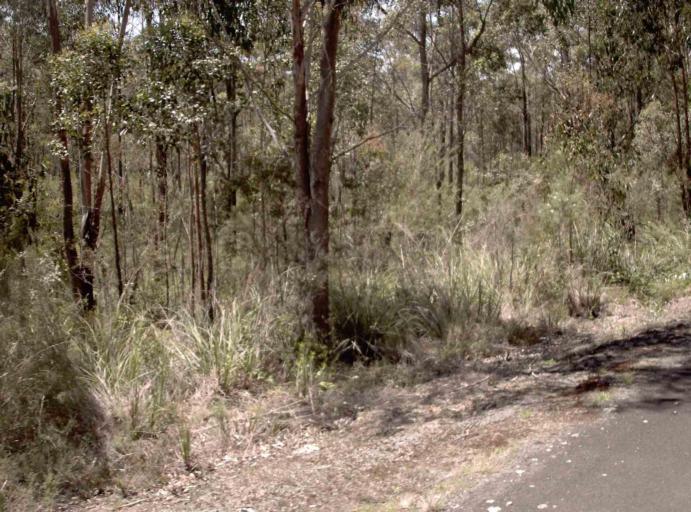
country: AU
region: Victoria
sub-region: East Gippsland
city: Lakes Entrance
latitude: -37.7093
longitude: 148.6845
